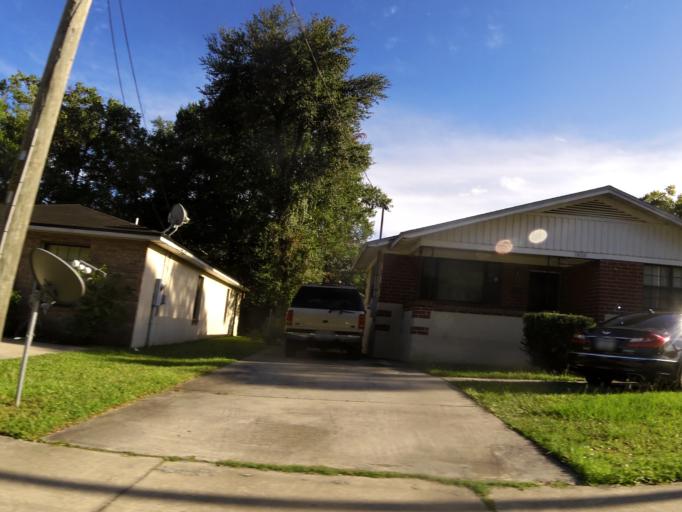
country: US
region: Florida
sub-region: Duval County
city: Jacksonville
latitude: 30.3513
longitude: -81.6783
